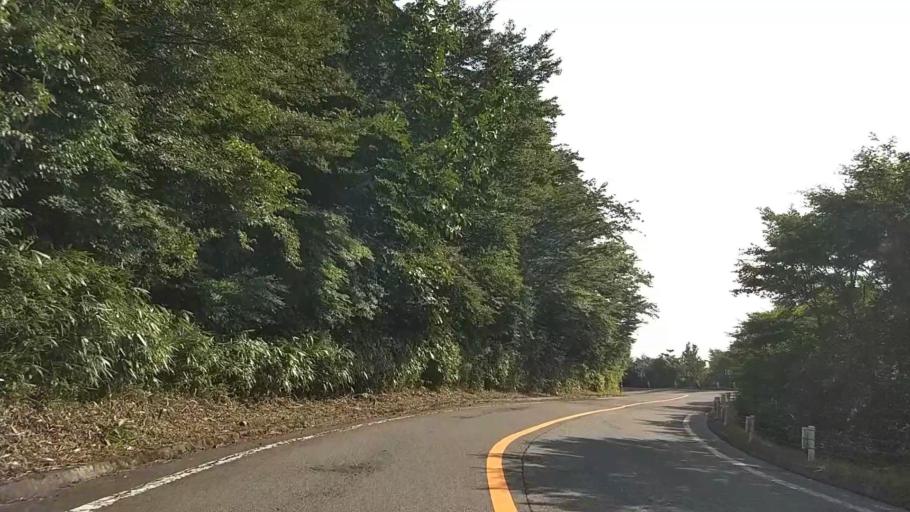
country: JP
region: Shizuoka
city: Gotemba
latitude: 35.2336
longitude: 138.9721
